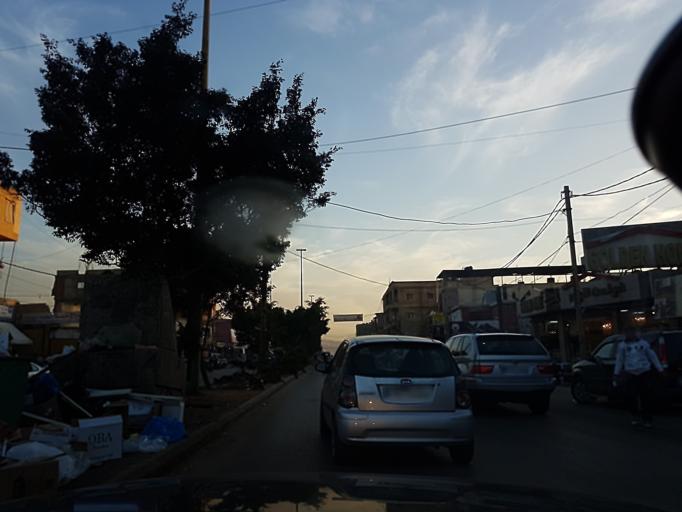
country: LB
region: Beyrouth
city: Beirut
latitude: 33.8352
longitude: 35.4846
